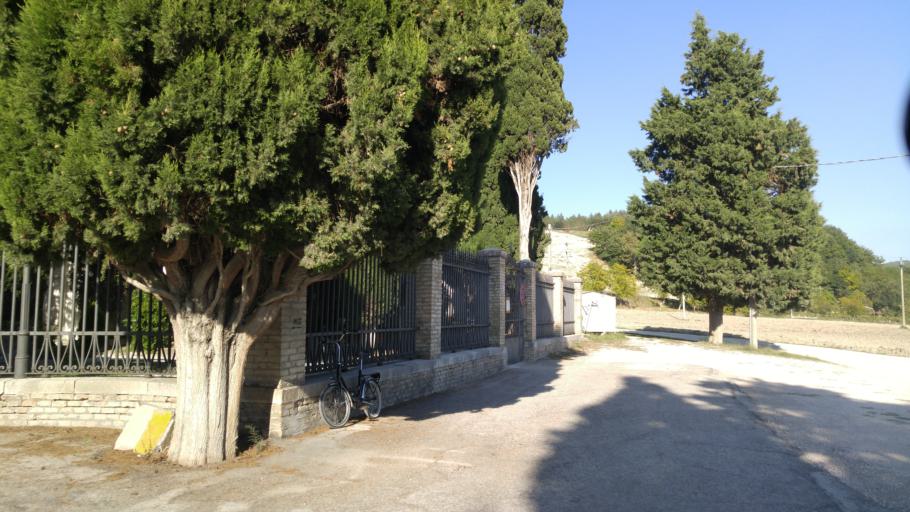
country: IT
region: The Marches
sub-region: Provincia di Pesaro e Urbino
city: Fermignano
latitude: 43.6725
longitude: 12.6339
